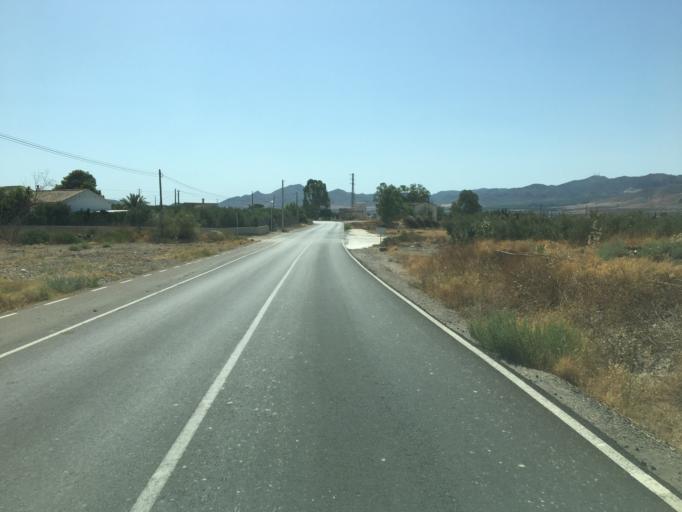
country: ES
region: Andalusia
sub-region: Provincia de Almeria
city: Huercal-Overa
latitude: 37.4200
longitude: -1.9161
